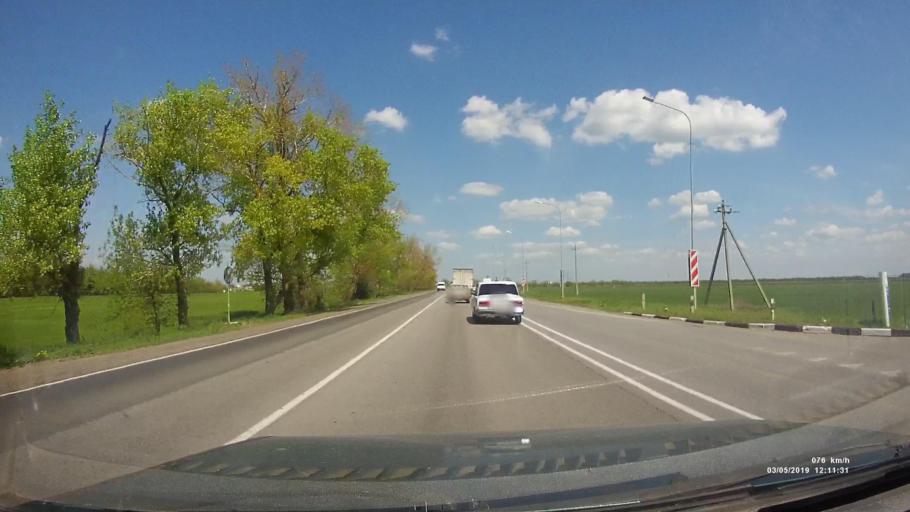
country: RU
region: Rostov
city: Bagayevskaya
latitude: 47.3117
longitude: 40.5393
